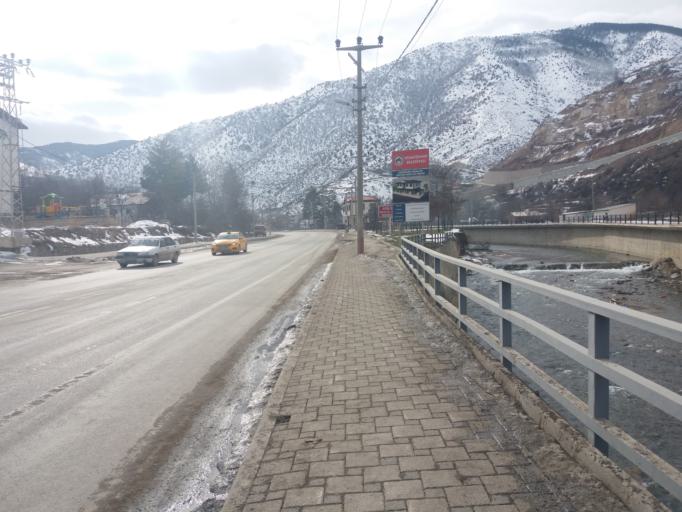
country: TR
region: Gumushane
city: Gumushkhane
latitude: 40.4444
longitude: 39.5036
